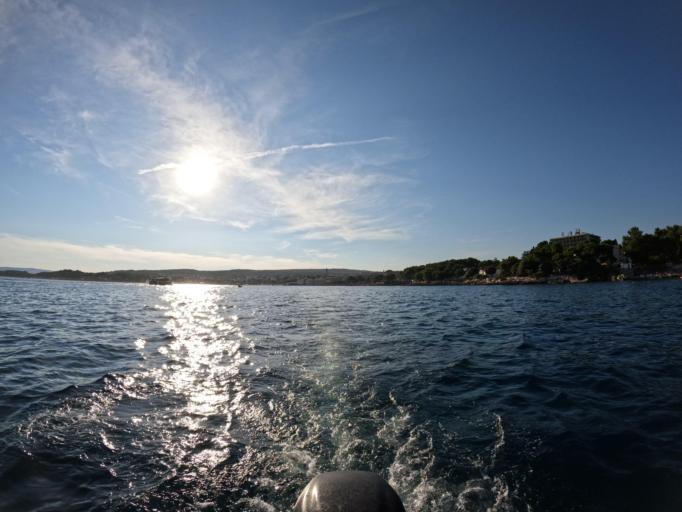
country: HR
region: Primorsko-Goranska
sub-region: Grad Krk
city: Krk
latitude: 45.0230
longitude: 14.5835
